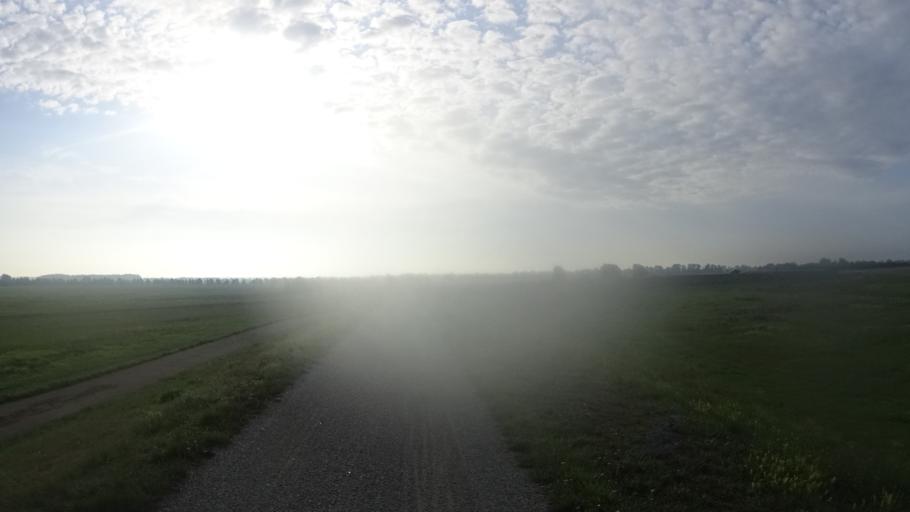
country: DE
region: Brandenburg
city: Lanz
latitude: 53.0555
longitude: 11.5637
